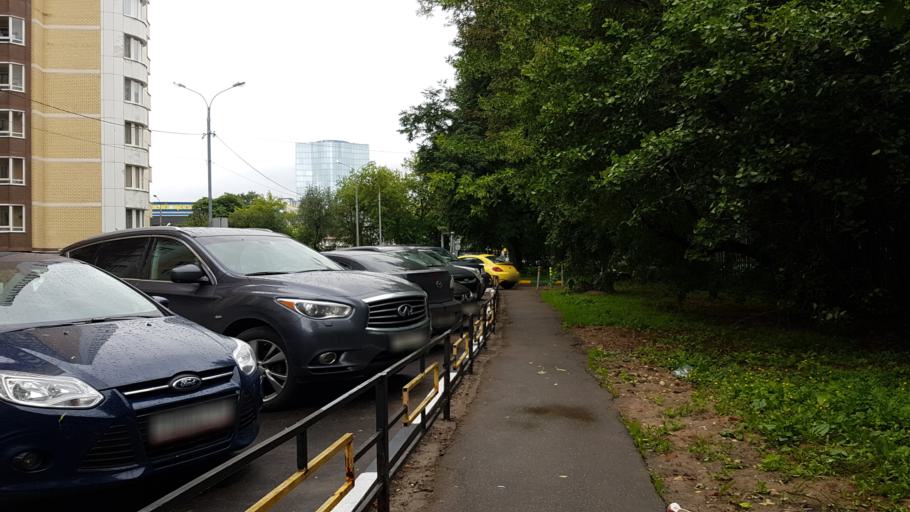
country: RU
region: Moscow
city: Khimki
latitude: 55.8884
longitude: 37.4560
